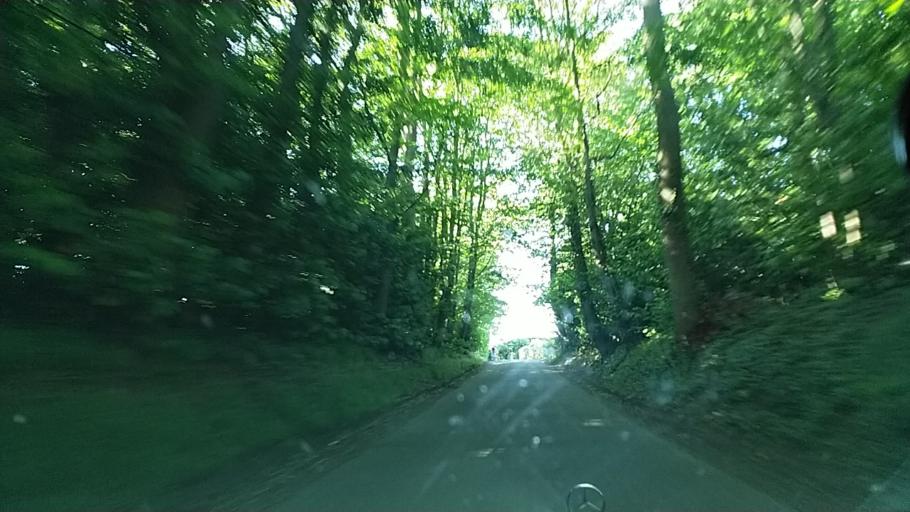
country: GB
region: England
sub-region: Warwickshire
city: Wroxall
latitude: 52.3049
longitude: -1.6375
